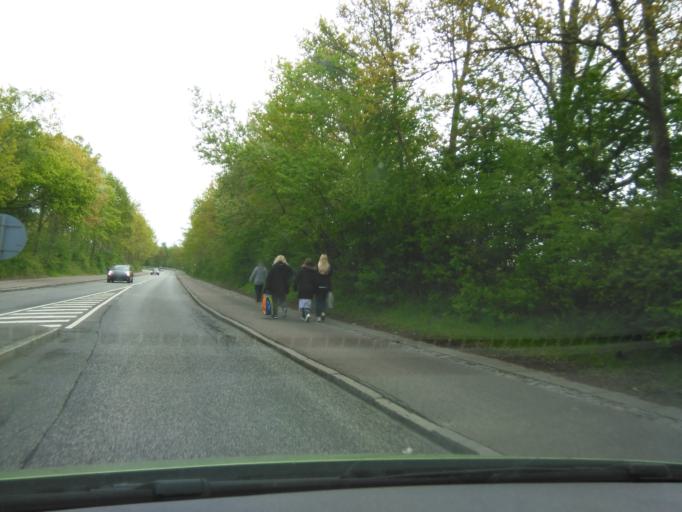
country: DK
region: Central Jutland
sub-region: Arhus Kommune
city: Arhus
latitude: 56.1892
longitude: 10.2008
